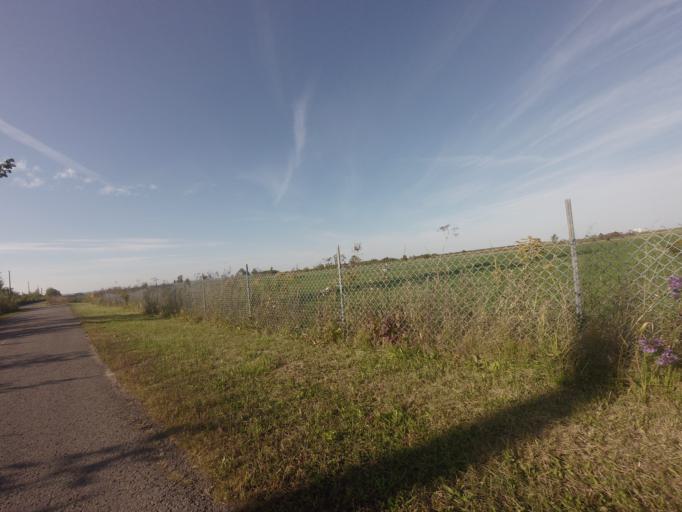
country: CA
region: Quebec
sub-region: Laurentides
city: Blainville
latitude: 45.7136
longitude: -73.9206
